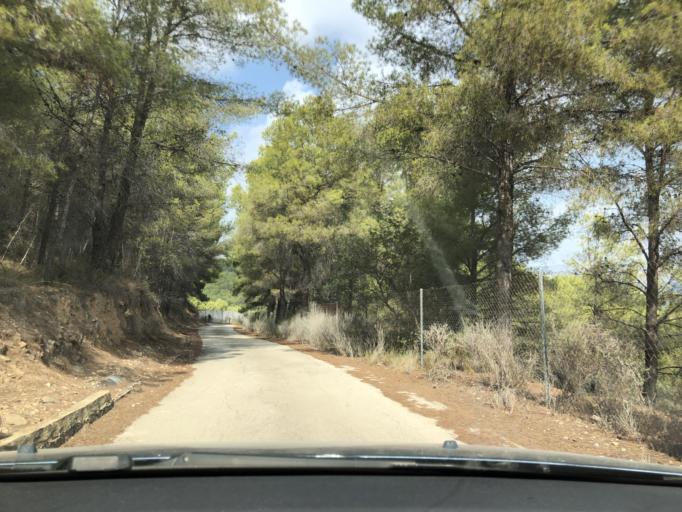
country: ES
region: Valencia
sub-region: Provincia de Alicante
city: Callosa d'En Sarria
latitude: 38.6346
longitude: -0.1073
